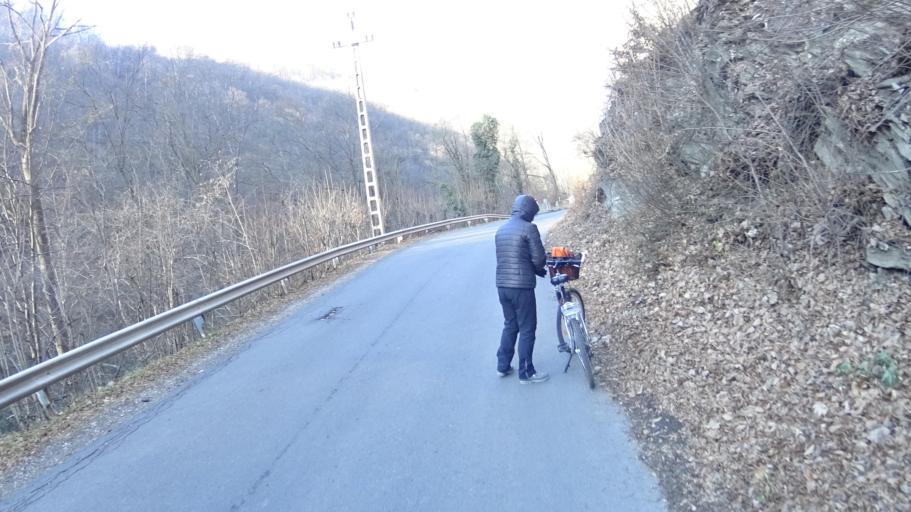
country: HU
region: Borsod-Abauj-Zemplen
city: Sajobabony
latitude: 48.1070
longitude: 20.6185
